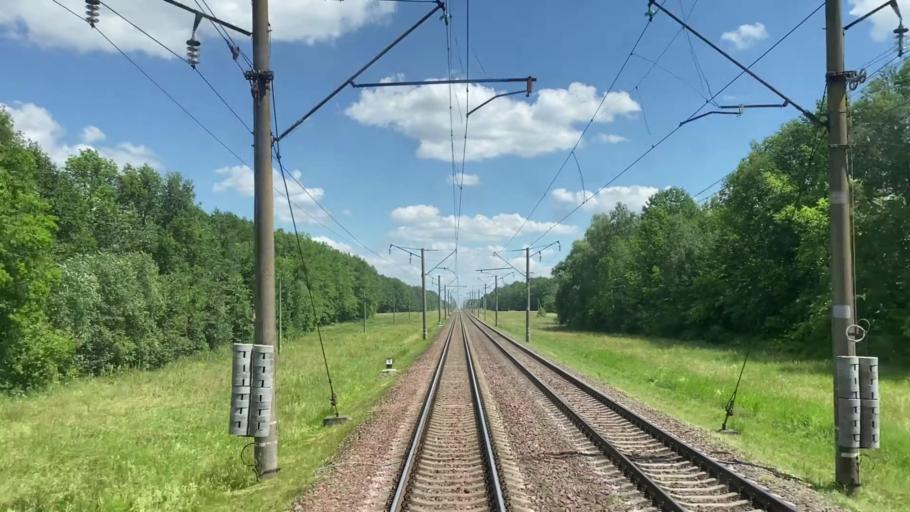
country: BY
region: Brest
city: Pruzhany
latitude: 52.5055
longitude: 24.6631
